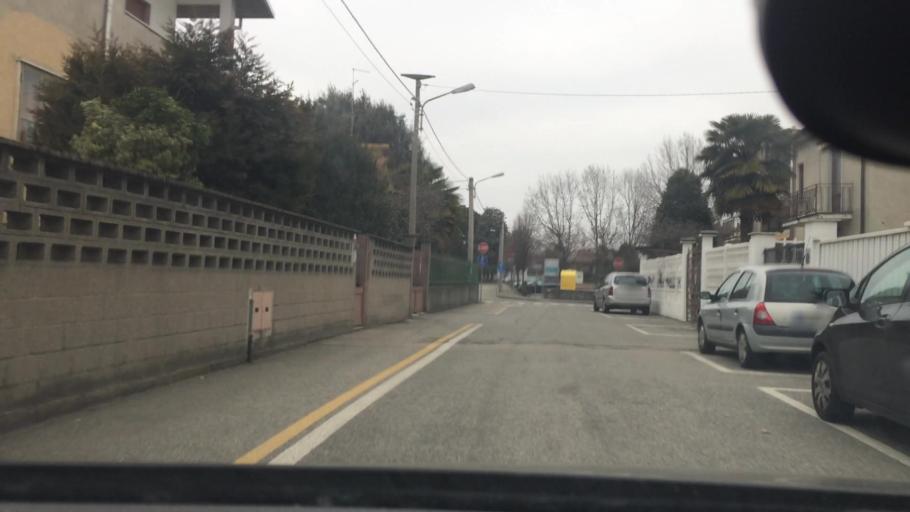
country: IT
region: Lombardy
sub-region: Citta metropolitana di Milano
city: Solaro
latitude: 45.6160
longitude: 9.0757
